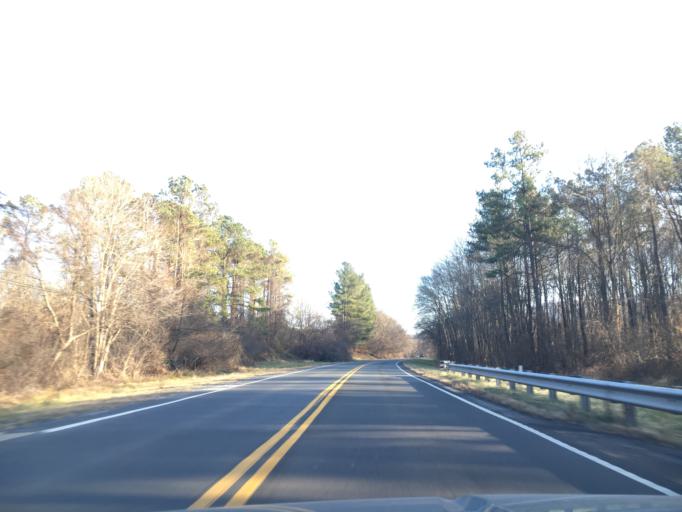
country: US
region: Virginia
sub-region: Warren County
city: Front Royal
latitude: 38.8841
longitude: -78.1649
